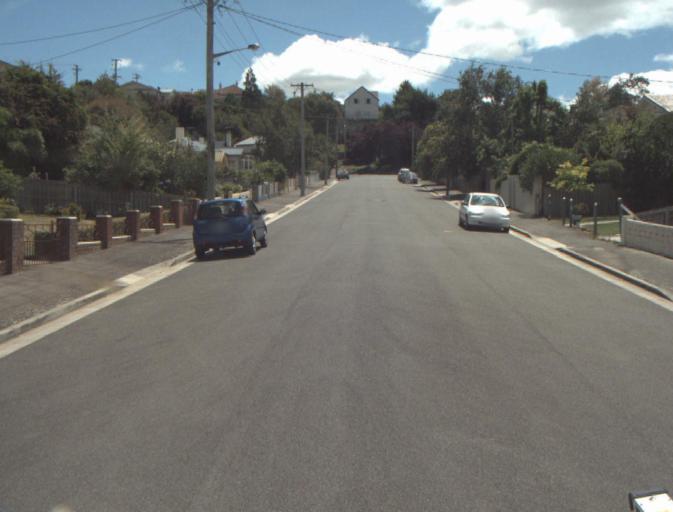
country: AU
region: Tasmania
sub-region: Launceston
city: East Launceston
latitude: -41.4420
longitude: 147.1565
